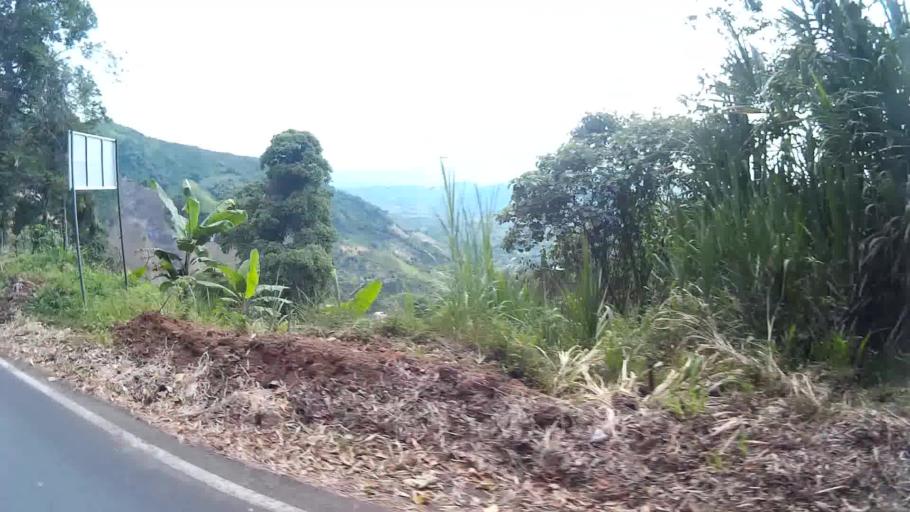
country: CO
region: Risaralda
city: Marsella
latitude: 4.8751
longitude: -75.7627
